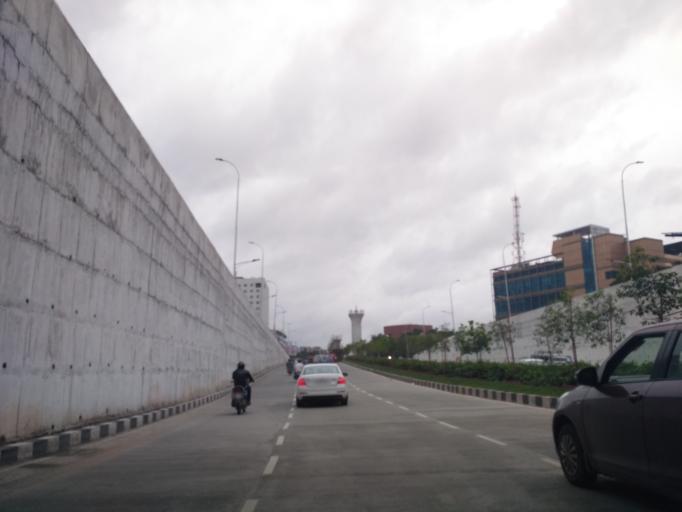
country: IN
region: Telangana
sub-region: Rangareddi
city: Kukatpalli
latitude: 17.4400
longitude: 78.3771
